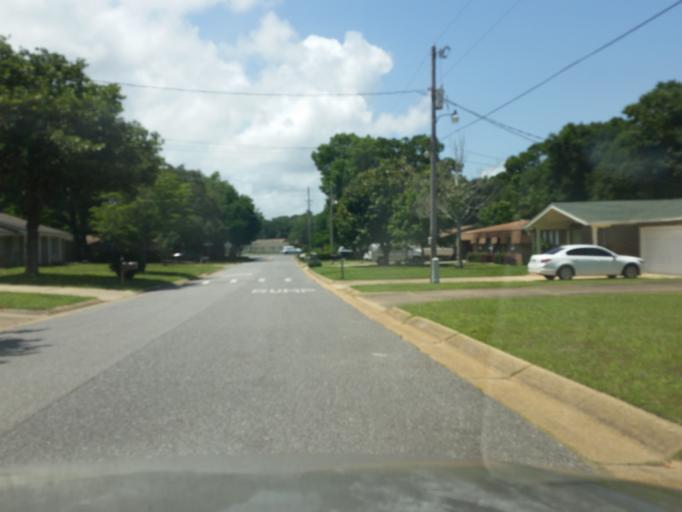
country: US
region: Florida
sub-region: Escambia County
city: Ferry Pass
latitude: 30.5141
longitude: -87.1781
